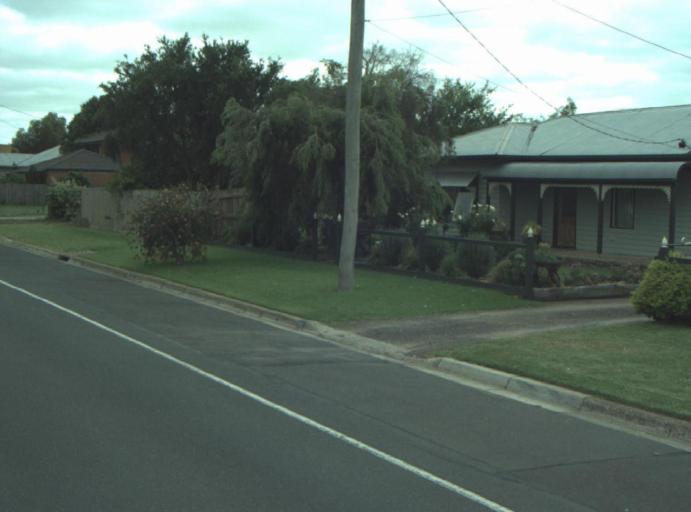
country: AU
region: Victoria
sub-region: Greater Geelong
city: Lara
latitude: -38.0302
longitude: 144.4129
